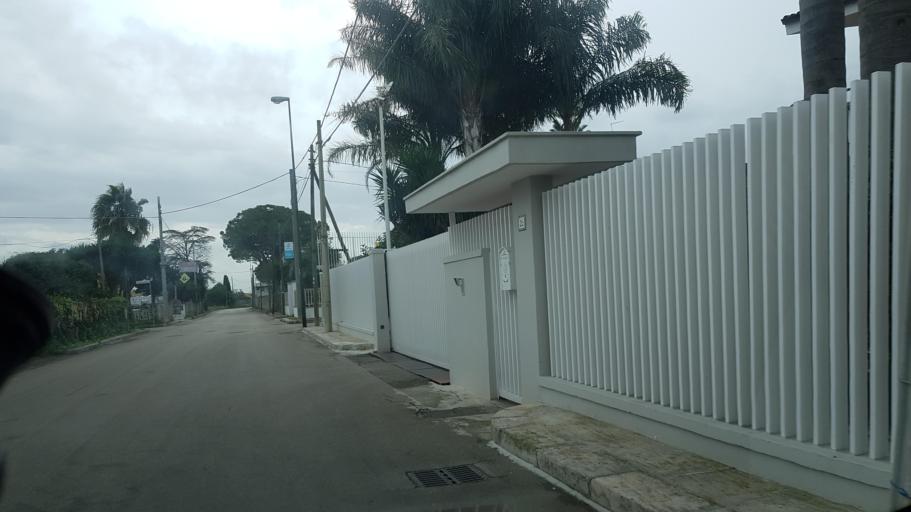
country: IT
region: Apulia
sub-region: Provincia di Lecce
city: Campi Salentina
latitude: 40.3925
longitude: 18.0187
